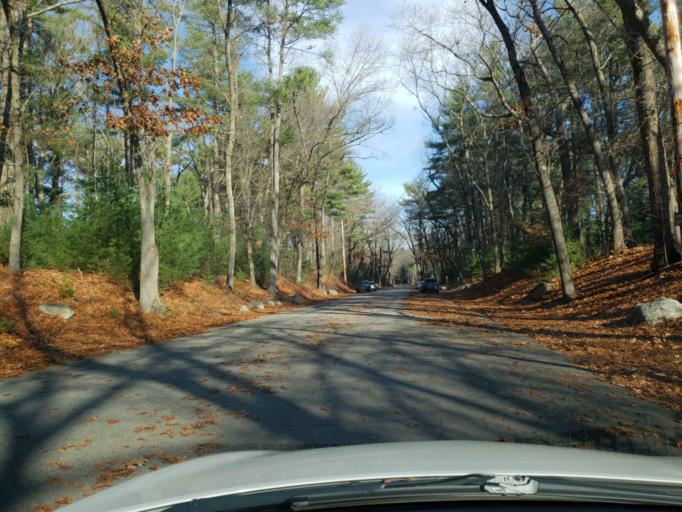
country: US
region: Massachusetts
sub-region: Essex County
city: Andover
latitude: 42.6320
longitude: -71.1482
